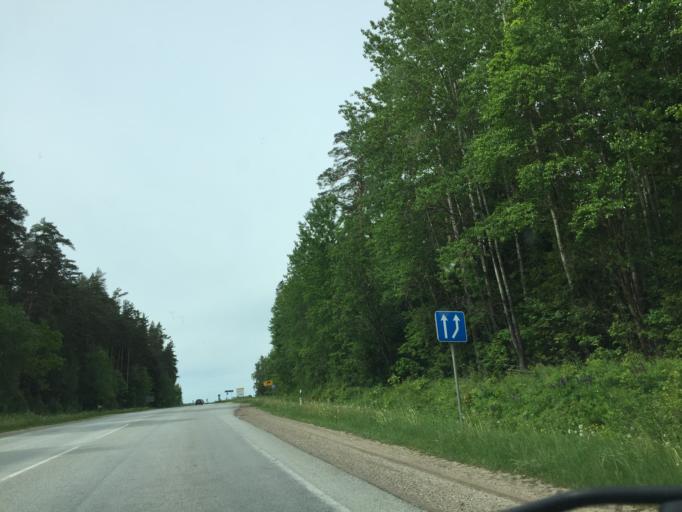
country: LV
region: Koceni
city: Koceni
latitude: 57.5179
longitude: 25.3786
